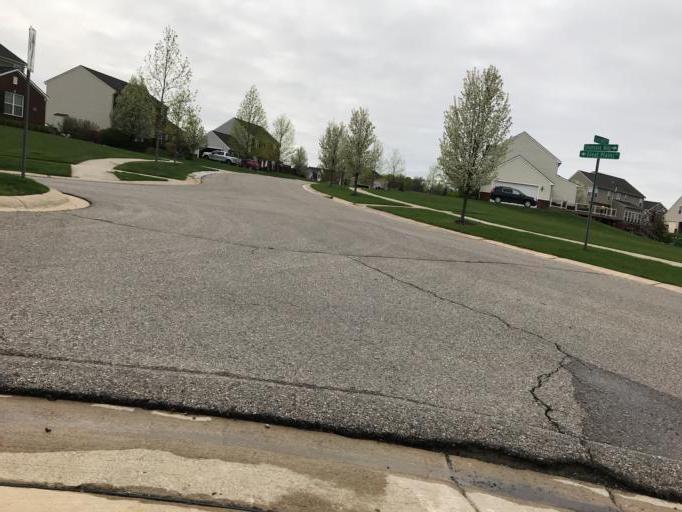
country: US
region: Michigan
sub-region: Oakland County
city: South Lyon
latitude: 42.4777
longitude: -83.6237
